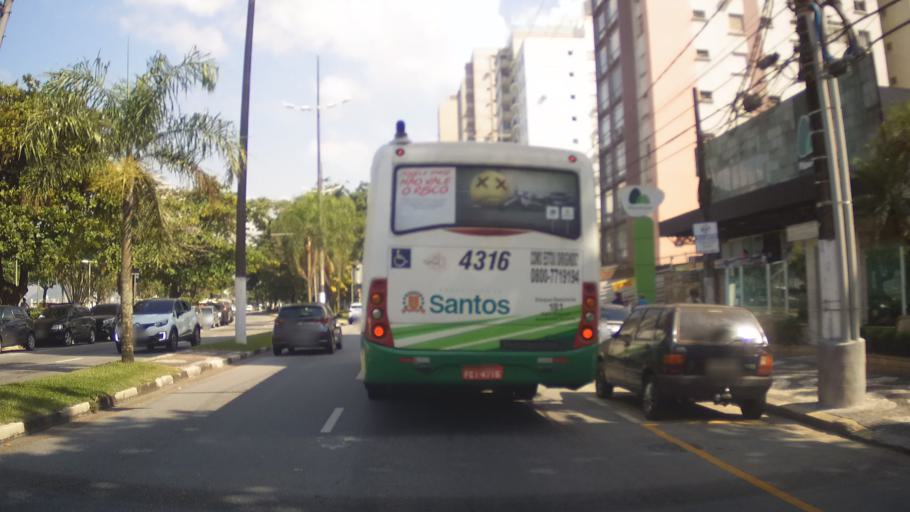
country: BR
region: Sao Paulo
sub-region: Santos
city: Santos
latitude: -23.9758
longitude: -46.3184
